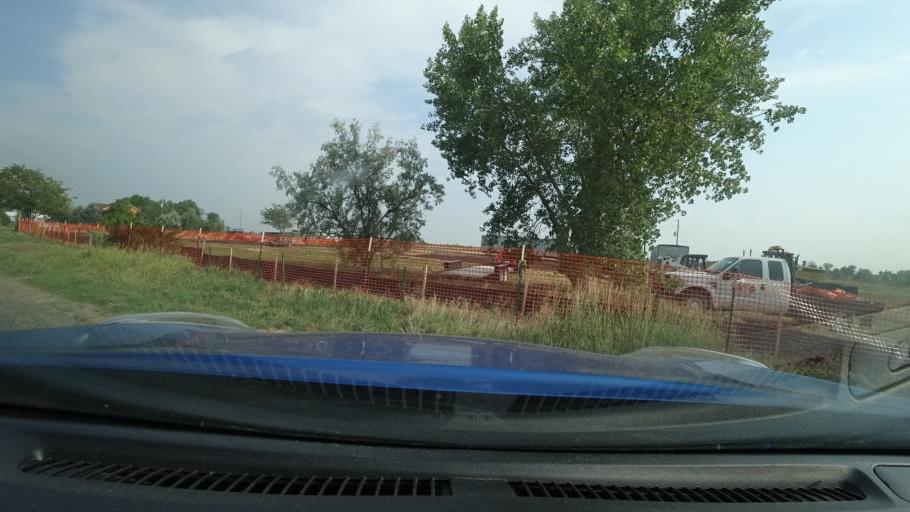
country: US
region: Colorado
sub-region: Adams County
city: Aurora
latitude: 39.7255
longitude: -104.7407
